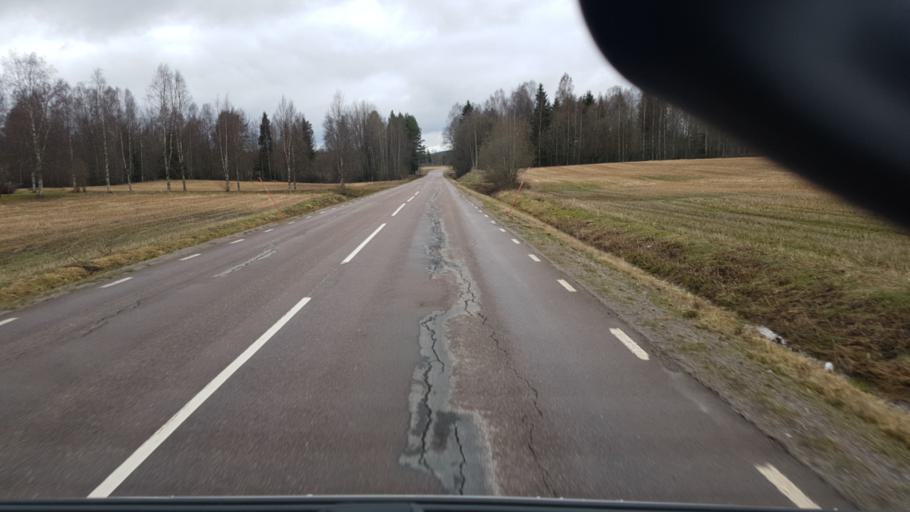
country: SE
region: Vaermland
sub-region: Eda Kommun
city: Charlottenberg
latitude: 59.9081
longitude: 12.2945
